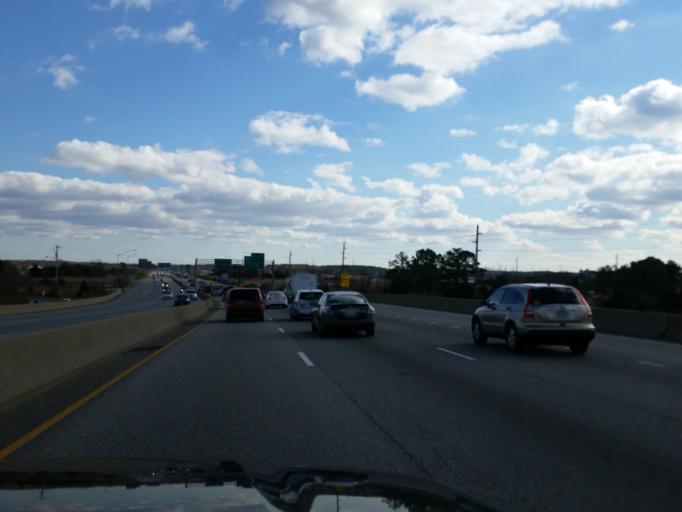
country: US
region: Maryland
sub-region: Queen Anne's County
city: Grasonville
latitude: 38.9690
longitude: -76.2399
